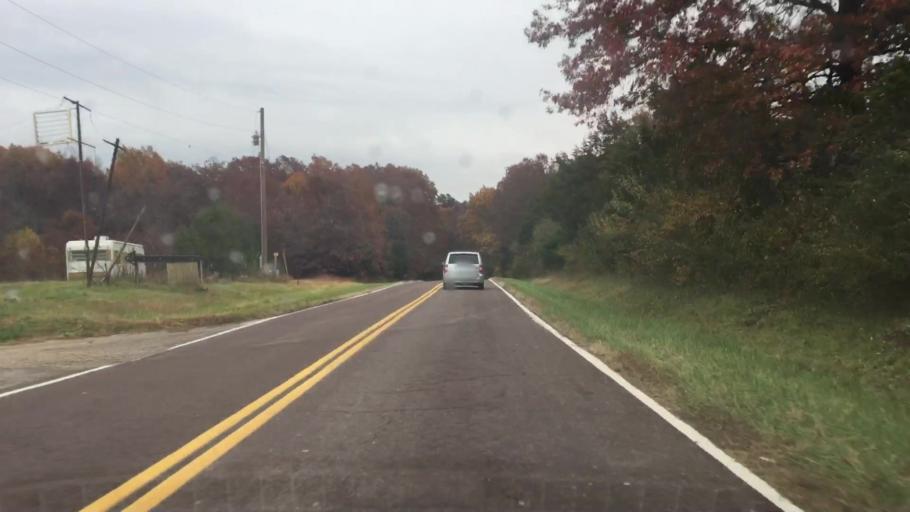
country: US
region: Missouri
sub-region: Callaway County
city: Fulton
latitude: 38.7869
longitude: -91.7637
